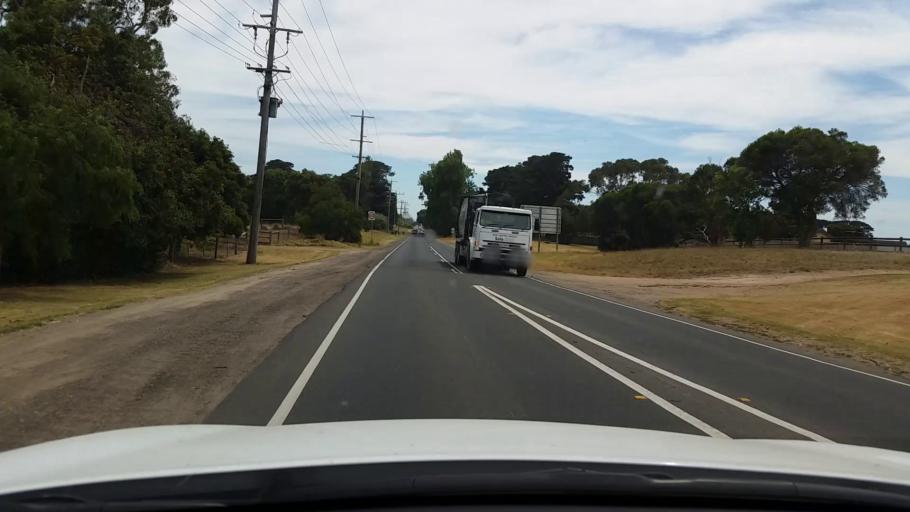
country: AU
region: Victoria
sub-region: Mornington Peninsula
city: Rosebud West
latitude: -38.3976
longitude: 144.8881
